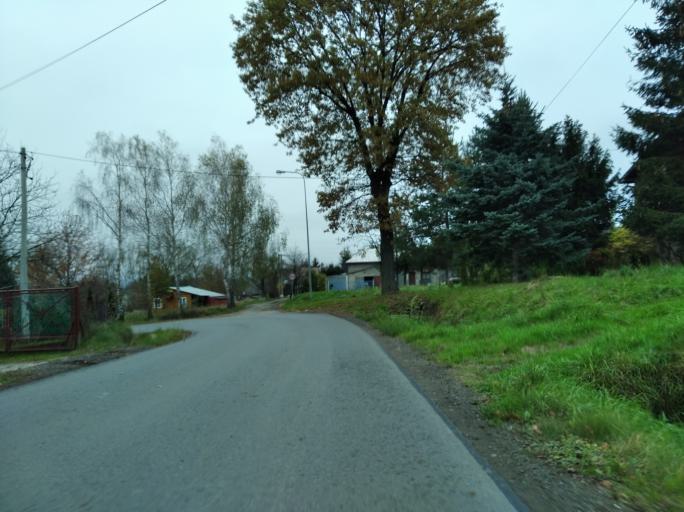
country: PL
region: Subcarpathian Voivodeship
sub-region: Powiat krosnienski
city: Jedlicze
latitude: 49.7317
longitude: 21.6508
